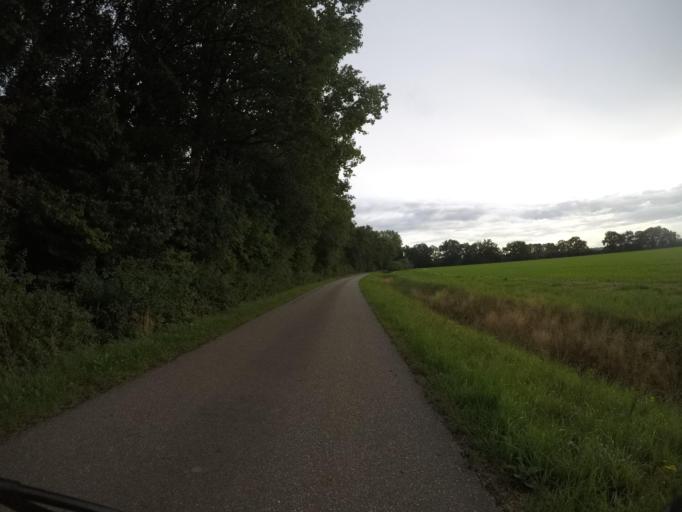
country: DE
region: Lower Saxony
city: Neu Darchau
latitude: 53.2739
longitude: 10.8814
